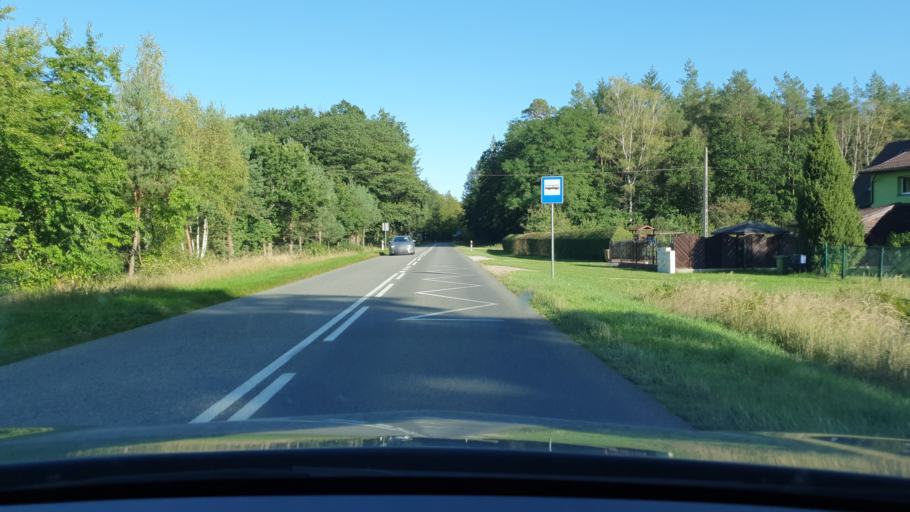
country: PL
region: West Pomeranian Voivodeship
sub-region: Powiat goleniowski
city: Przybiernow
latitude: 53.8272
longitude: 14.7861
